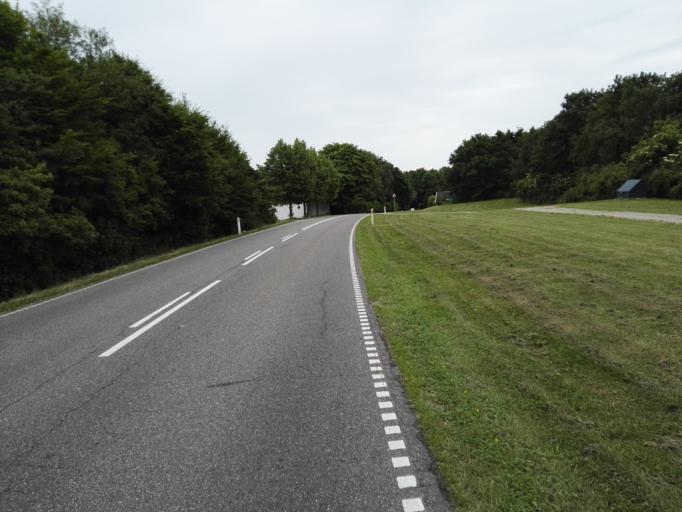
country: DK
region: Zealand
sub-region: Roskilde Kommune
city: Jyllinge
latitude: 55.7741
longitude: 12.1299
